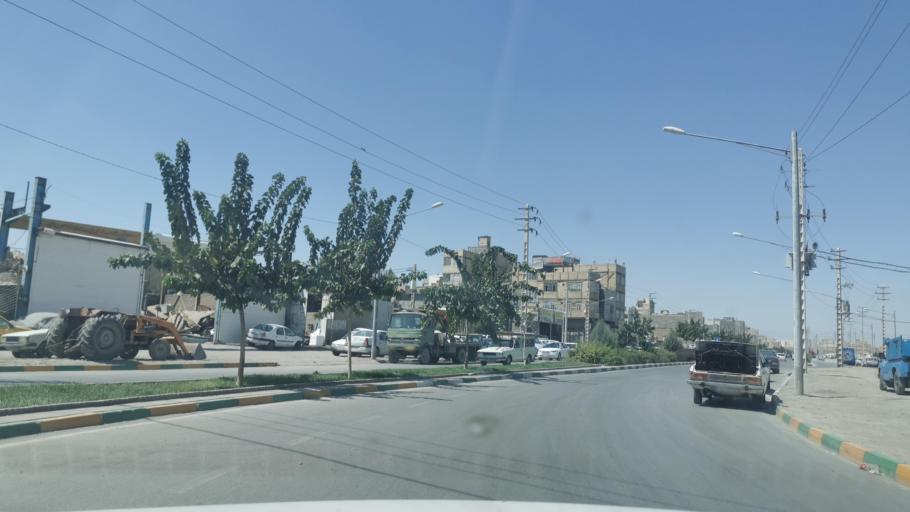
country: IR
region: Razavi Khorasan
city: Mashhad
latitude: 36.3541
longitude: 59.5699
